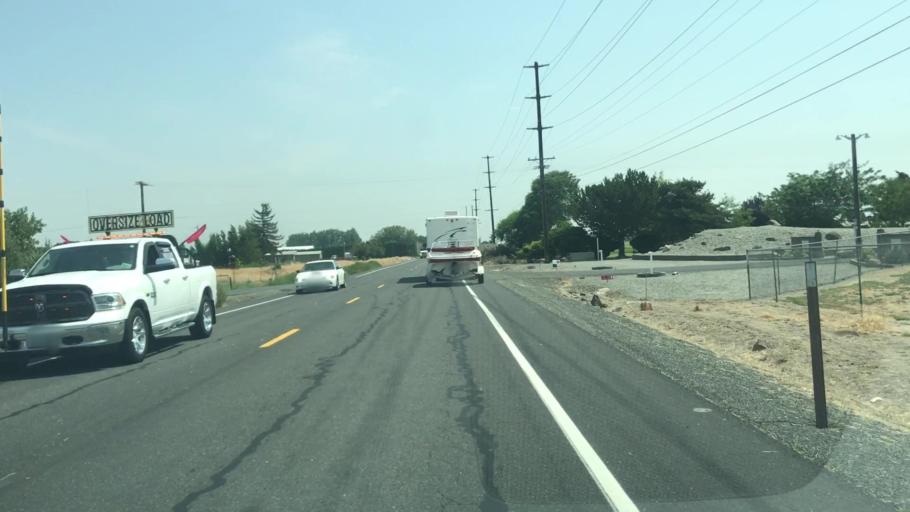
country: US
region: Washington
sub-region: Grant County
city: Quincy
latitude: 47.1613
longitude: -119.8692
